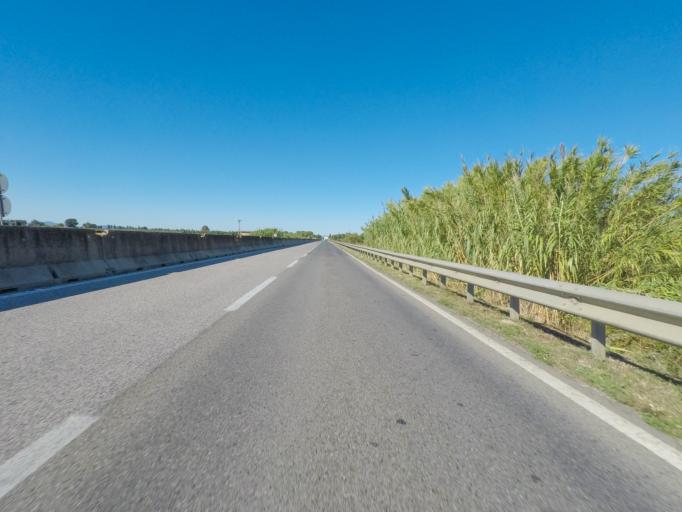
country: IT
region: Tuscany
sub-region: Provincia di Grosseto
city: Grosseto
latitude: 42.6816
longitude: 11.1400
